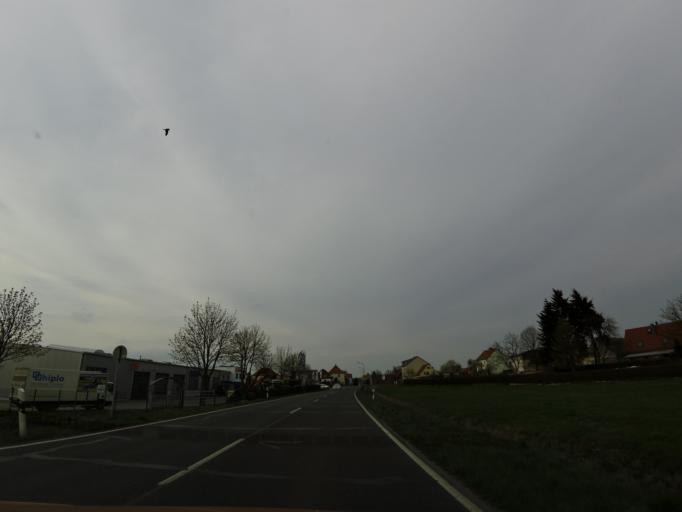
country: DE
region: Brandenburg
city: Mittenwalde
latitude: 52.2628
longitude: 13.5317
